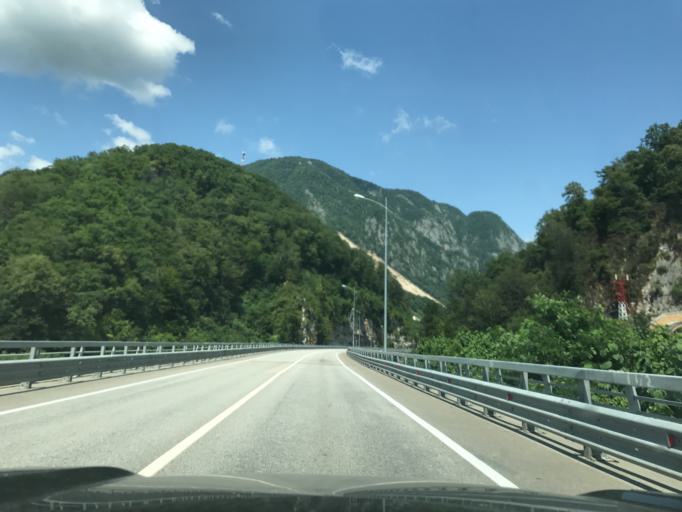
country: RU
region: Krasnodarskiy
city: Vysokoye
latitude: 43.5805
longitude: 40.0091
